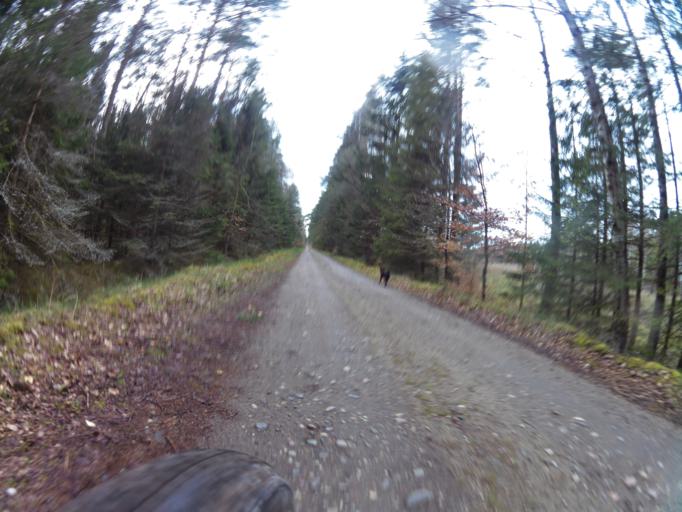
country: PL
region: West Pomeranian Voivodeship
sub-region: Powiat slawienski
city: Slawno
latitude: 54.3197
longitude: 16.7806
